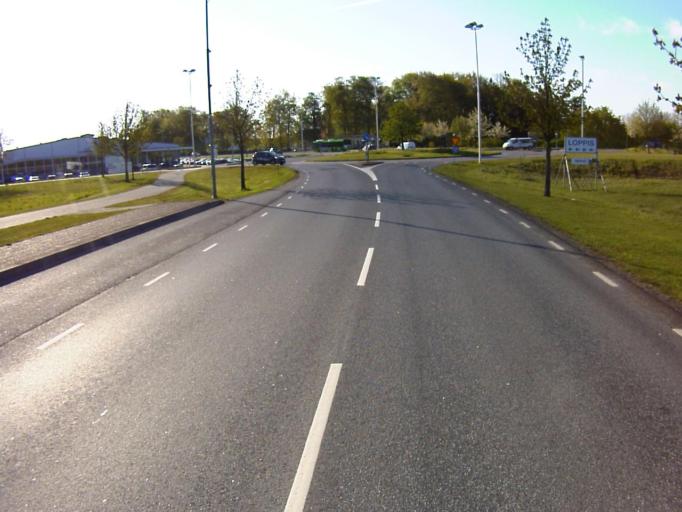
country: SE
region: Skane
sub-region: Kristianstads Kommun
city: Kristianstad
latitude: 56.0211
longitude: 14.1233
